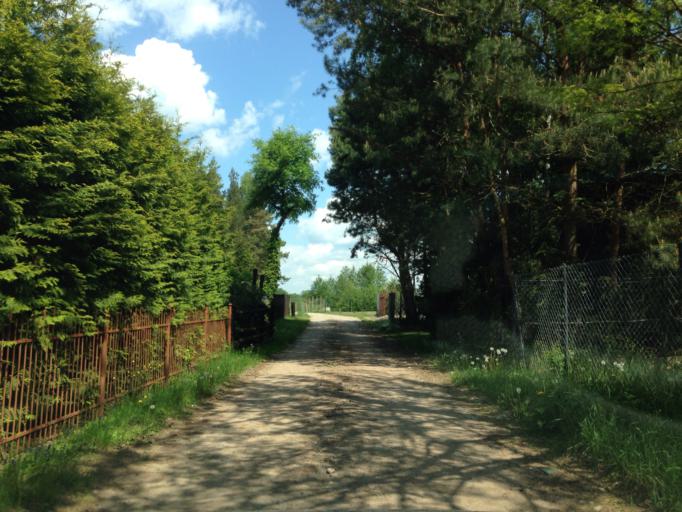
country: PL
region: Kujawsko-Pomorskie
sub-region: Powiat brodnicki
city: Brodnica
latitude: 53.3339
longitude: 19.3560
